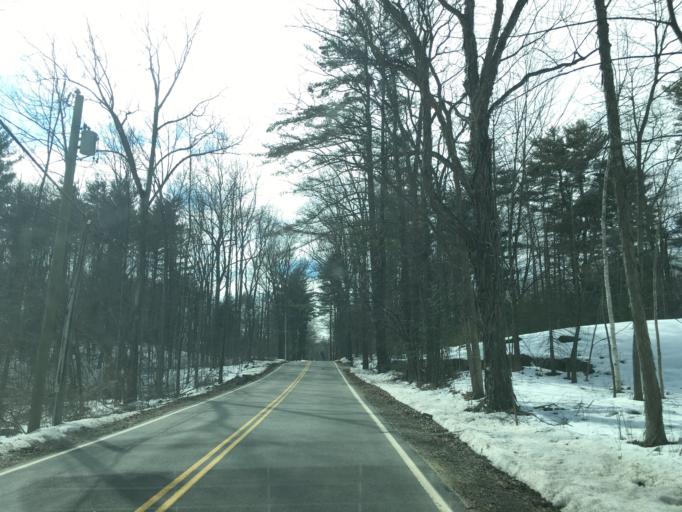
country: US
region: New Hampshire
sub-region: Rockingham County
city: North Hampton
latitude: 42.9928
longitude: -70.8708
